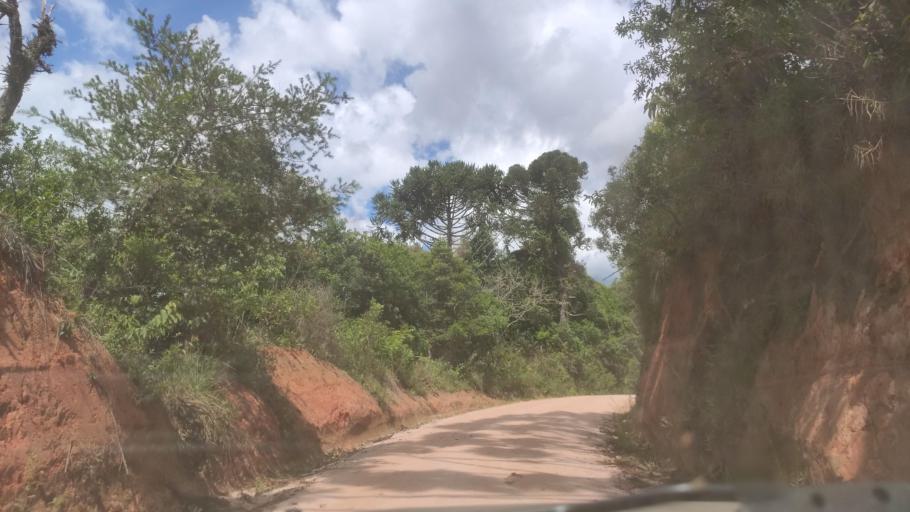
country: BR
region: Minas Gerais
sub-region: Camanducaia
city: Camanducaia
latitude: -22.7681
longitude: -45.9855
